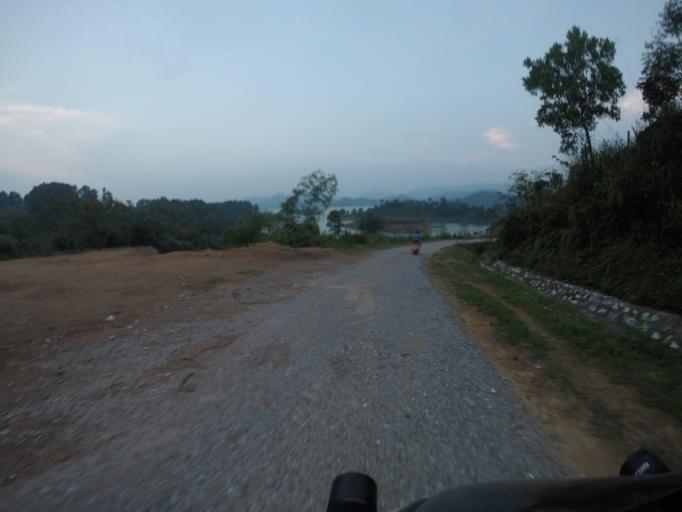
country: VN
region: Thai Nguyen
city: Chua Hang
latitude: 21.5843
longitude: 105.7100
